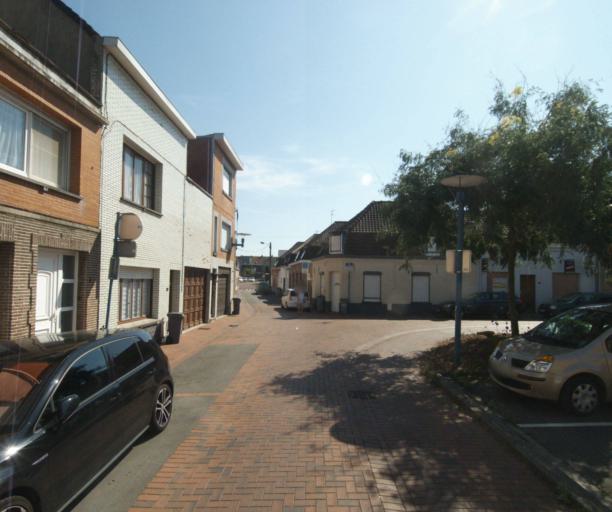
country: FR
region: Nord-Pas-de-Calais
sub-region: Departement du Nord
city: Halluin
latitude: 50.7864
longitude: 3.1296
